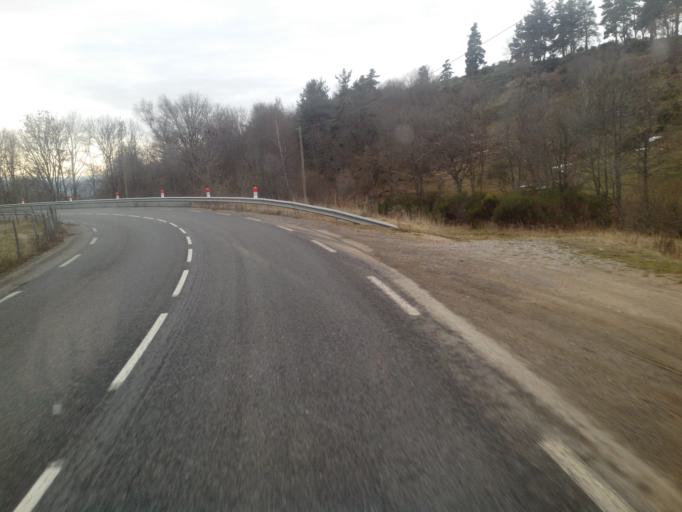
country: FR
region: Languedoc-Roussillon
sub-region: Departement de la Lozere
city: Mende
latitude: 44.5860
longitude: 3.4922
